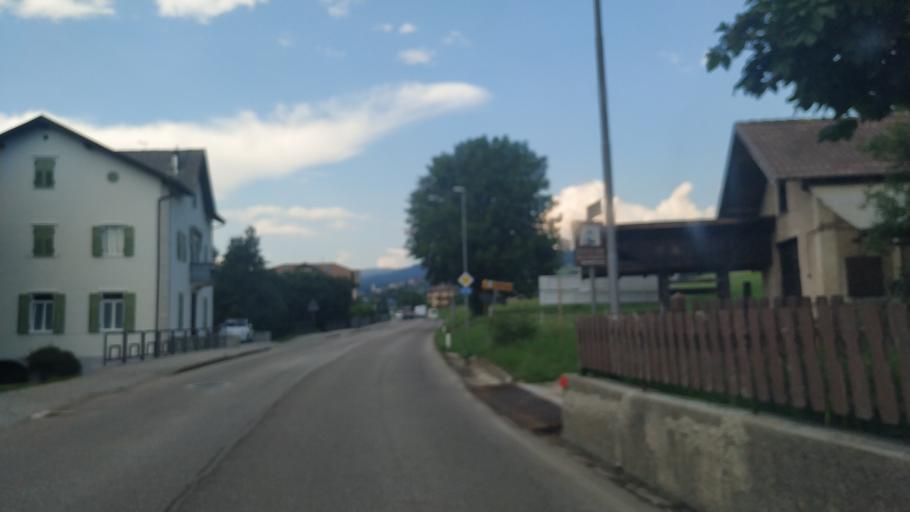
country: IT
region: Trentino-Alto Adige
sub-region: Provincia di Trento
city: Sarnonico
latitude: 46.4210
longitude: 11.1409
